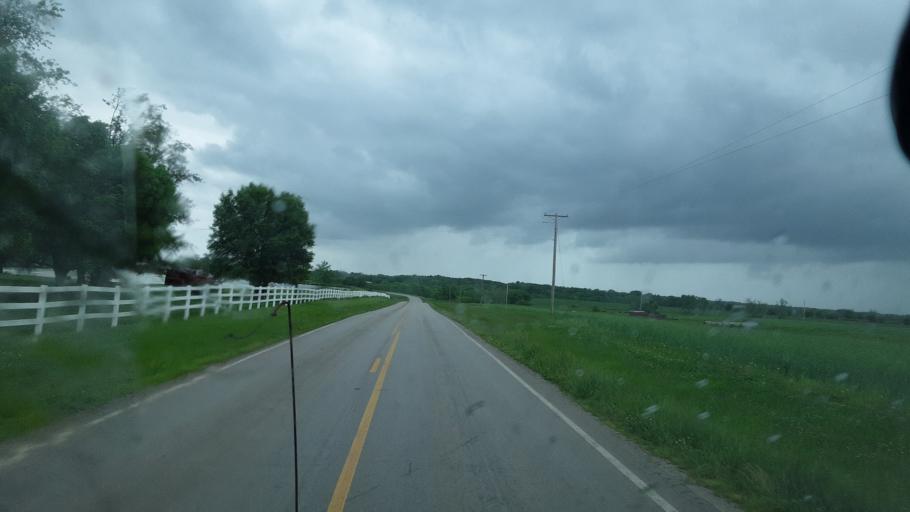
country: US
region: Missouri
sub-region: Monroe County
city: Paris
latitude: 39.4632
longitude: -92.2127
